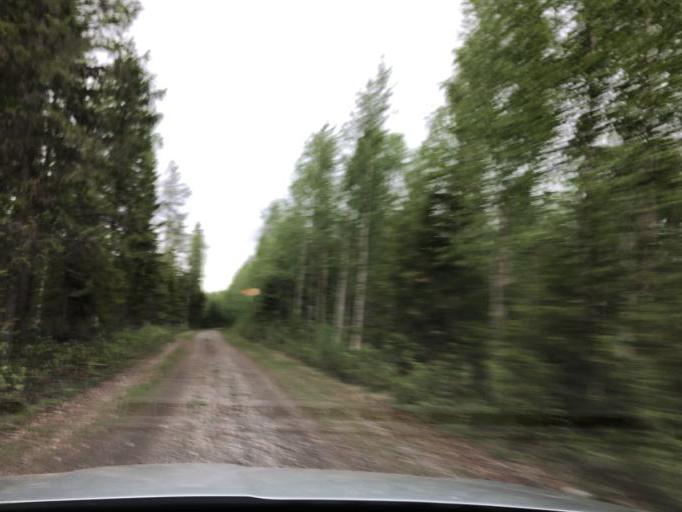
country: SE
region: Norrbotten
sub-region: Pitea Kommun
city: Roknas
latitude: 65.4018
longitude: 21.2622
